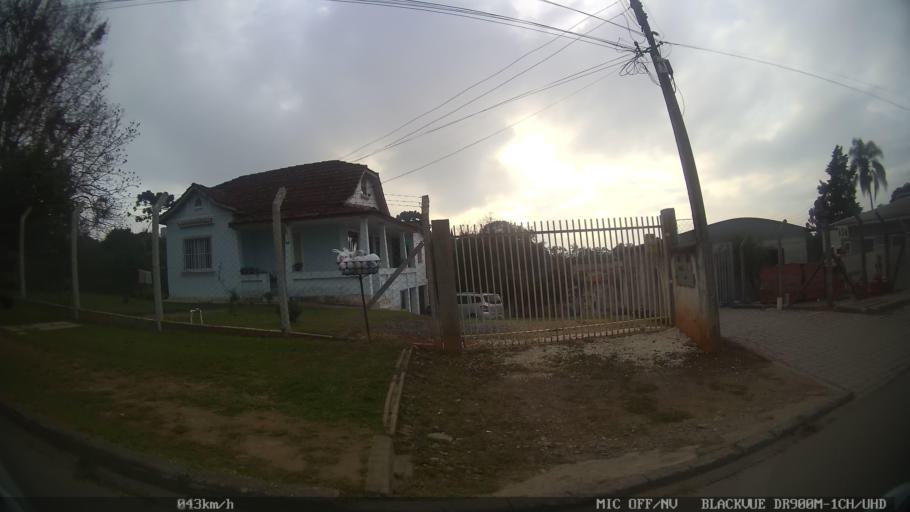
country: BR
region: Parana
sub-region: Almirante Tamandare
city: Almirante Tamandare
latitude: -25.3779
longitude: -49.3161
